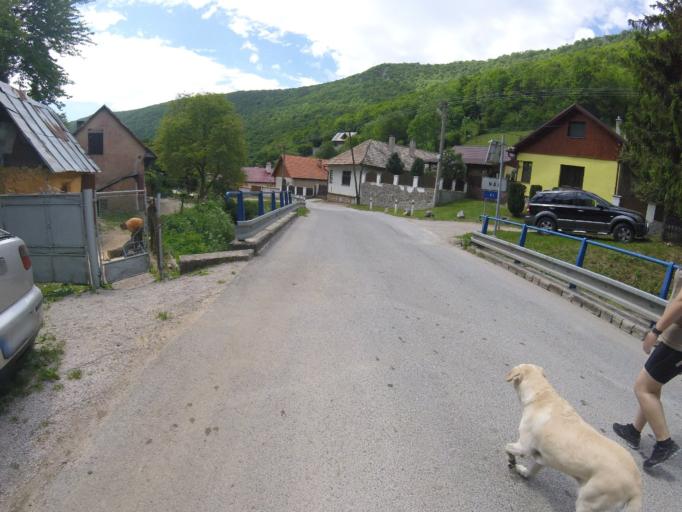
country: SK
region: Kosicky
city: Medzev
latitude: 48.6348
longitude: 20.8507
